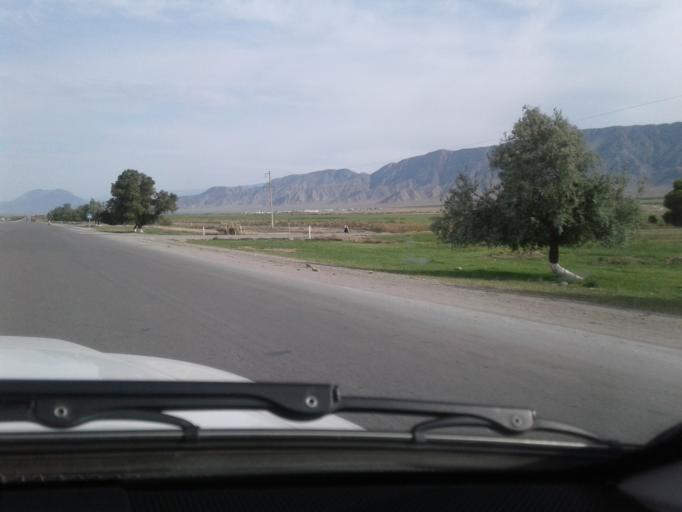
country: TM
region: Ahal
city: Arcabil
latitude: 38.2063
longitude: 57.8192
